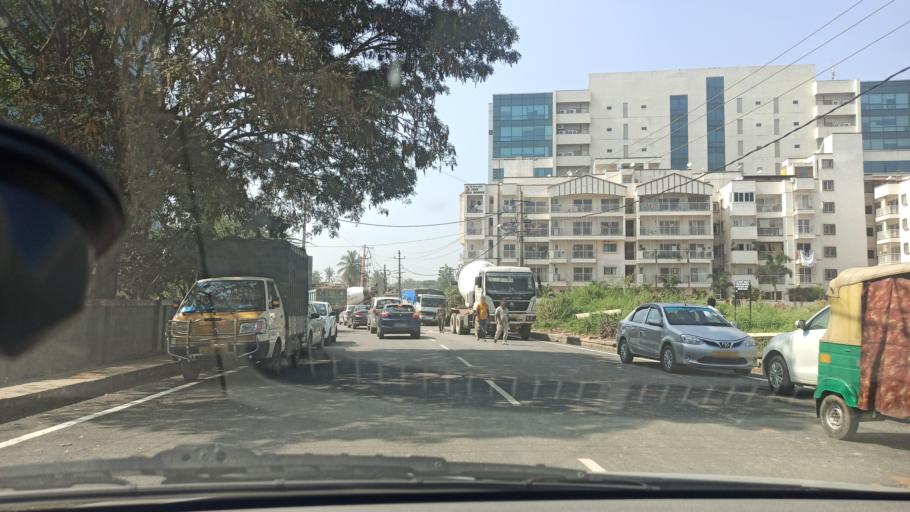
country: IN
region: Karnataka
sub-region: Bangalore Urban
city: Bangalore
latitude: 12.9399
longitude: 77.6910
